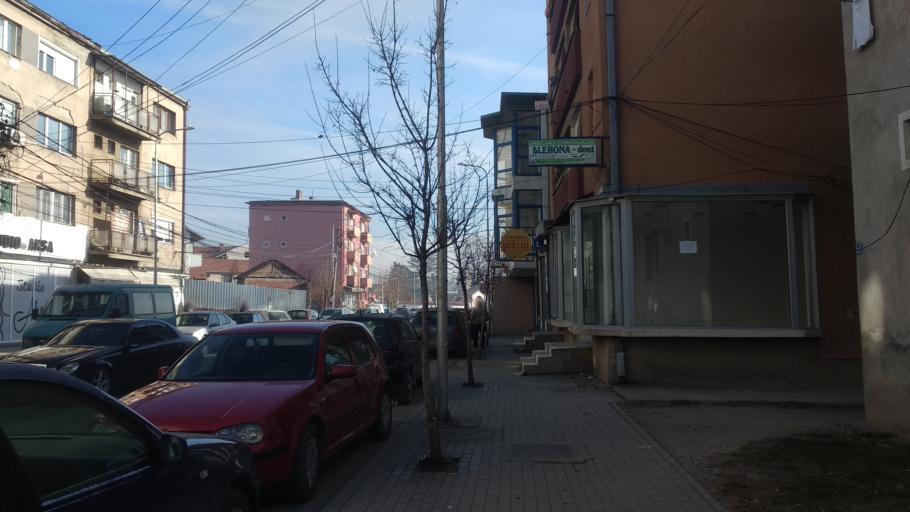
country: XK
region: Mitrovica
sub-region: Vushtrri
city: Vushtrri
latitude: 42.8213
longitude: 20.9728
